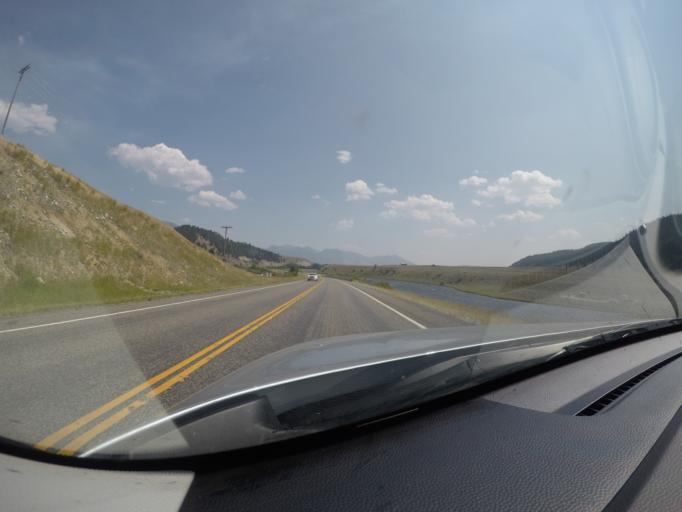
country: US
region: Montana
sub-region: Gallatin County
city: Big Sky
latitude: 44.8687
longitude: -111.5610
